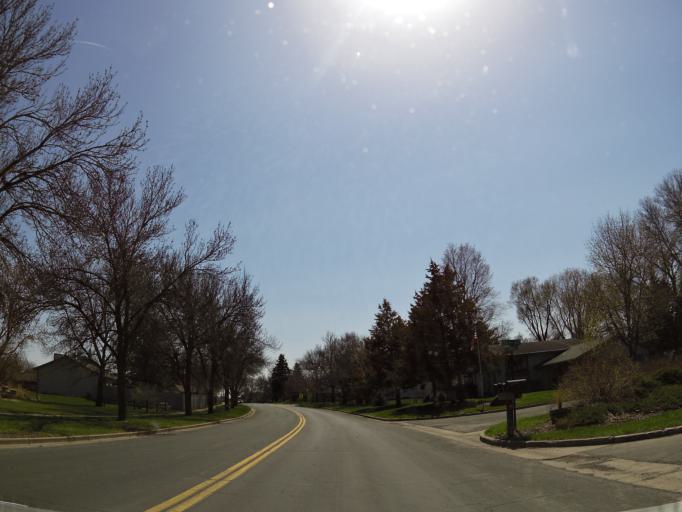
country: US
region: Wisconsin
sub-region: Saint Croix County
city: Hudson
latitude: 44.9671
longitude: -92.7352
